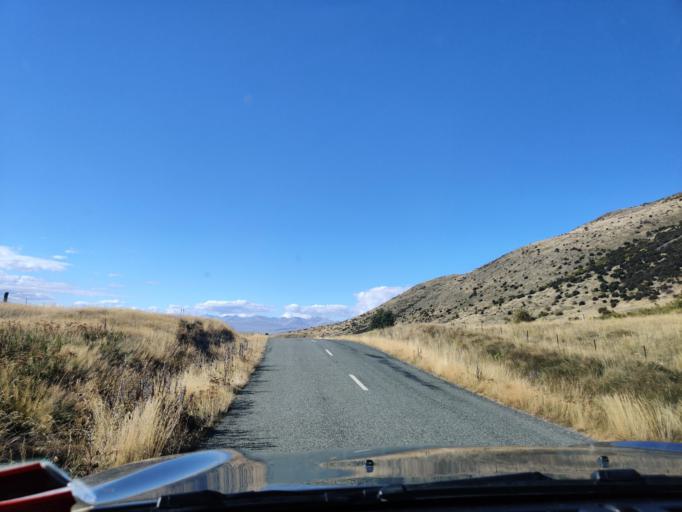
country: NZ
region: Canterbury
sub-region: Timaru District
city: Pleasant Point
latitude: -43.9817
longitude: 170.4591
